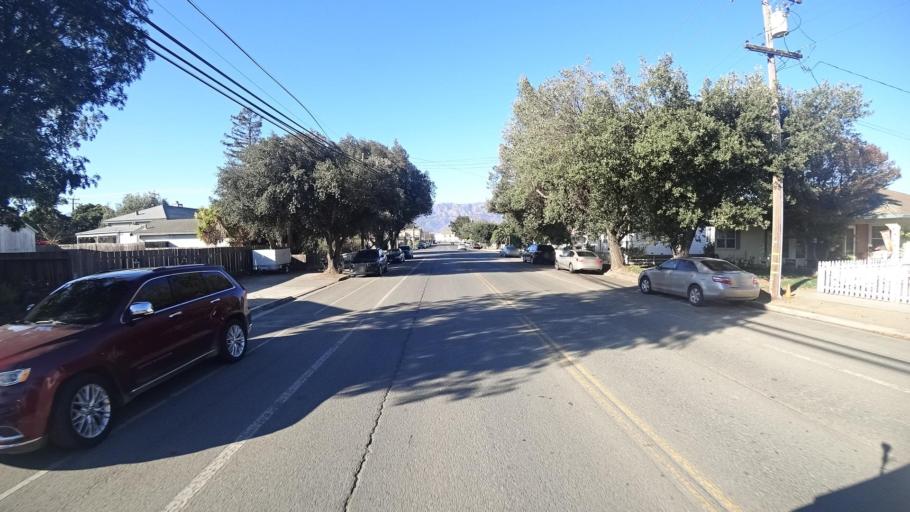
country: US
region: California
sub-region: Monterey County
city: Gonzales
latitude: 36.5086
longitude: -121.4443
